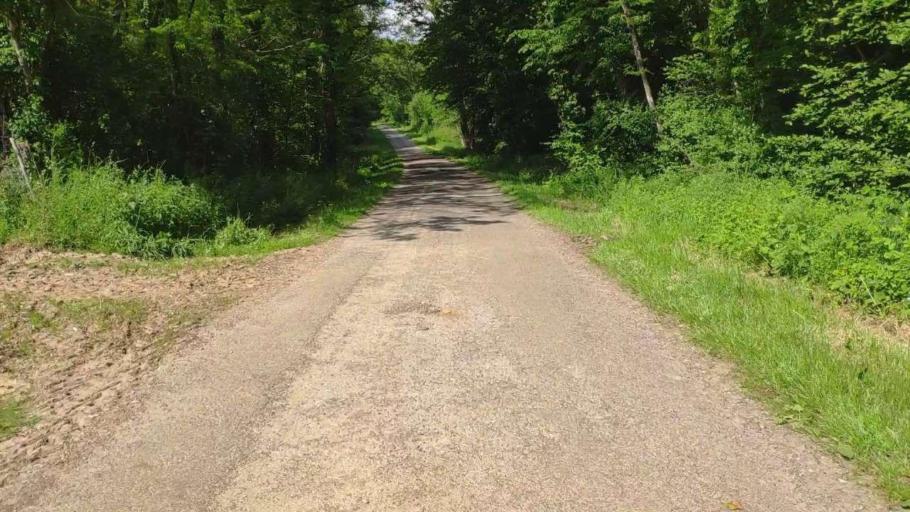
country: FR
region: Franche-Comte
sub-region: Departement du Jura
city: Bletterans
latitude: 46.8311
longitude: 5.4095
